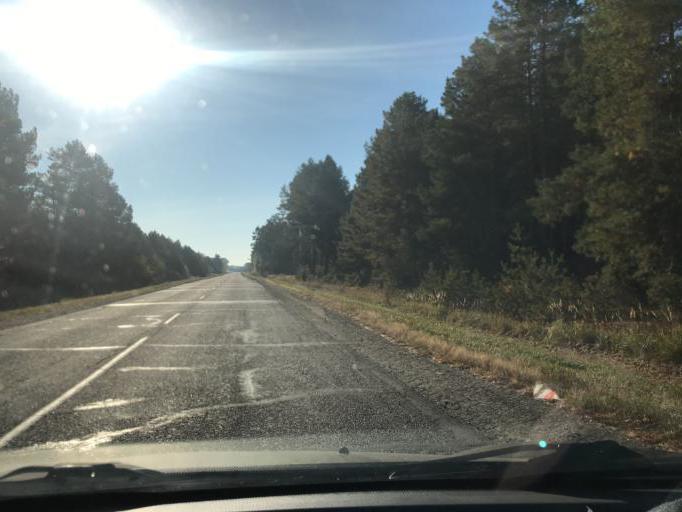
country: BY
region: Gomel
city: Brahin
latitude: 51.7485
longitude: 30.3137
